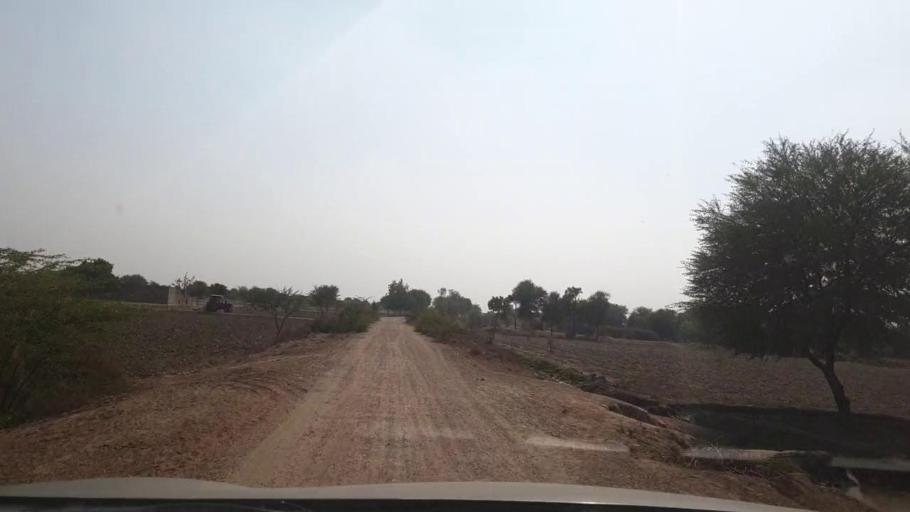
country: PK
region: Sindh
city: Tando Allahyar
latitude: 25.5594
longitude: 68.8347
